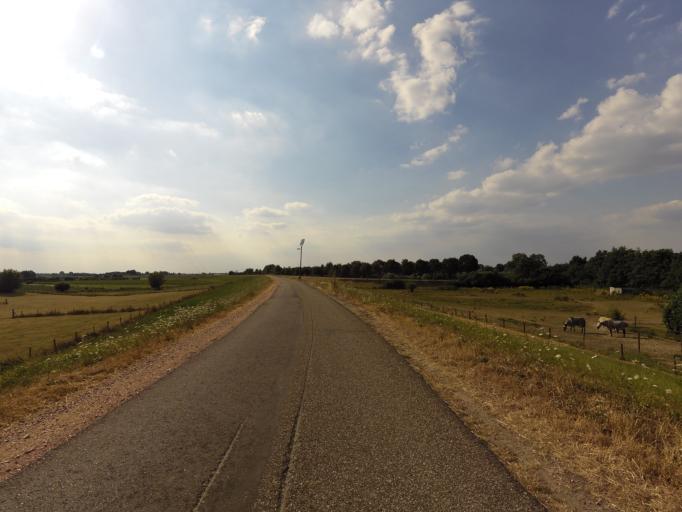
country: NL
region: Gelderland
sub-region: Gemeente Zevenaar
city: Zevenaar
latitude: 51.8836
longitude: 6.0930
